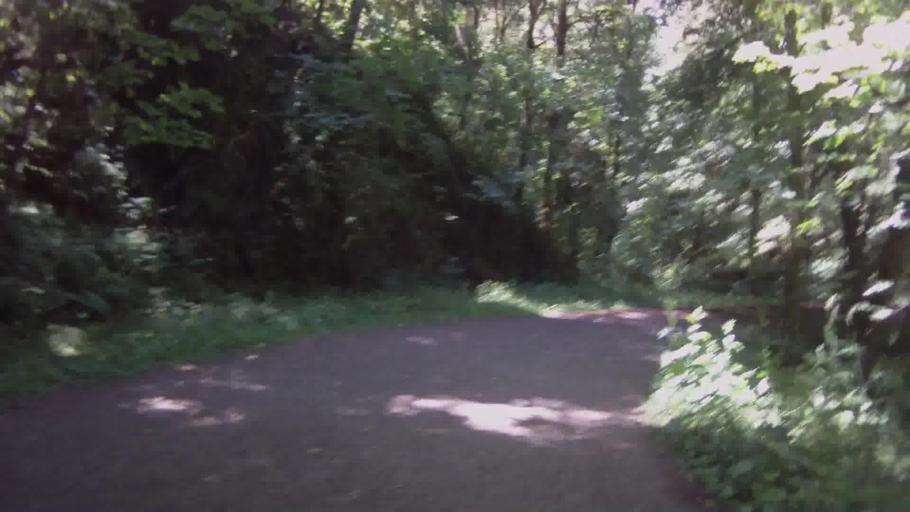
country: US
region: Oregon
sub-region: Washington County
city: West Haven-Sylvan
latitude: 45.5444
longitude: -122.7349
